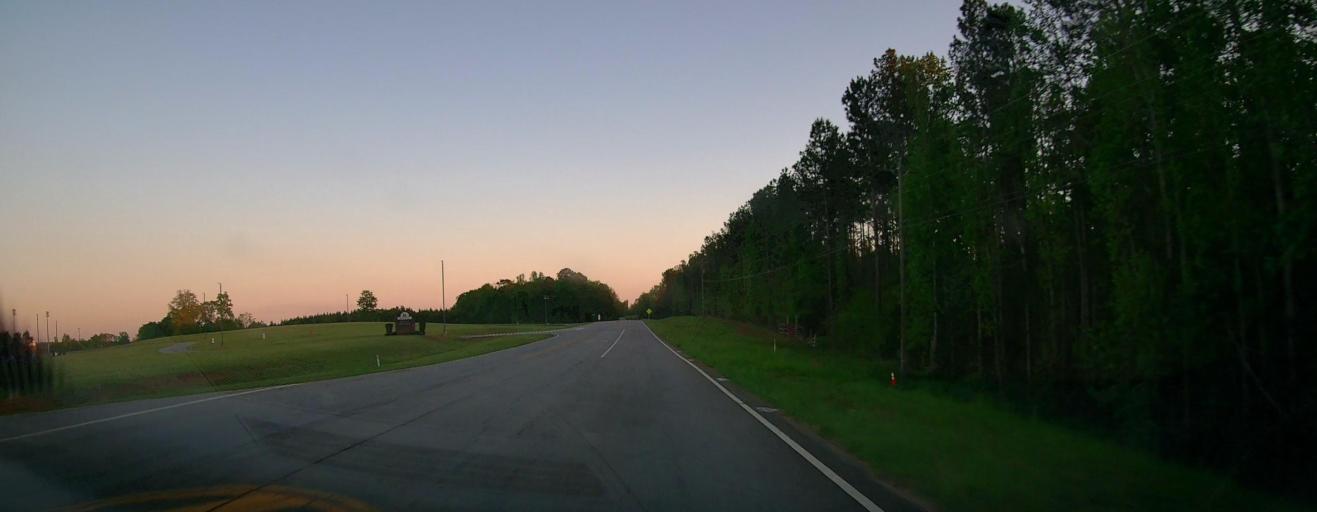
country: US
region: Georgia
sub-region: Marion County
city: Buena Vista
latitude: 32.3640
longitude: -84.5393
